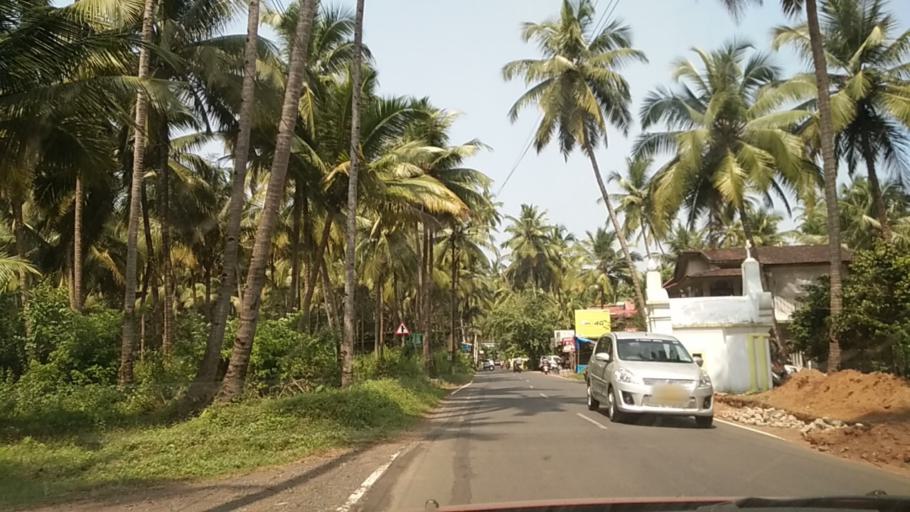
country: IN
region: Goa
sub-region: South Goa
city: Sancoale
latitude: 15.3364
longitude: 73.9009
